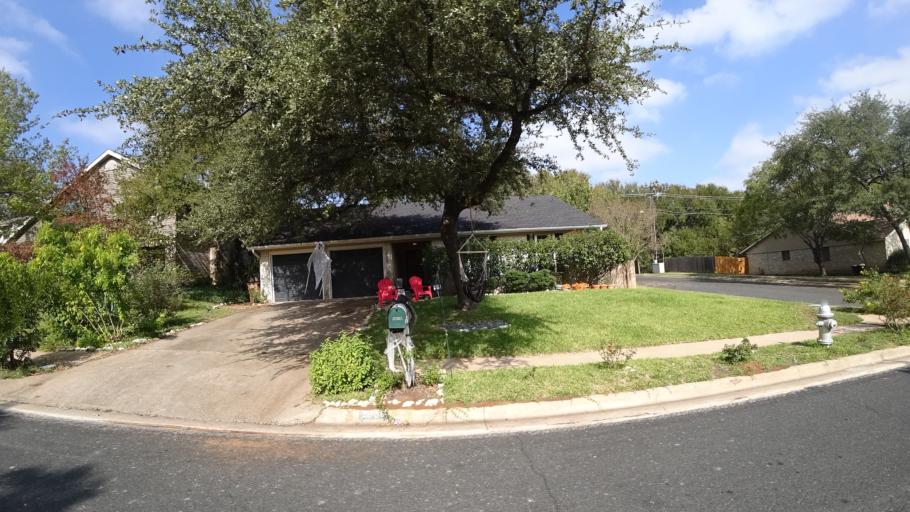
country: US
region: Texas
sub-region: Travis County
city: Shady Hollow
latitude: 30.2024
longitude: -97.8226
